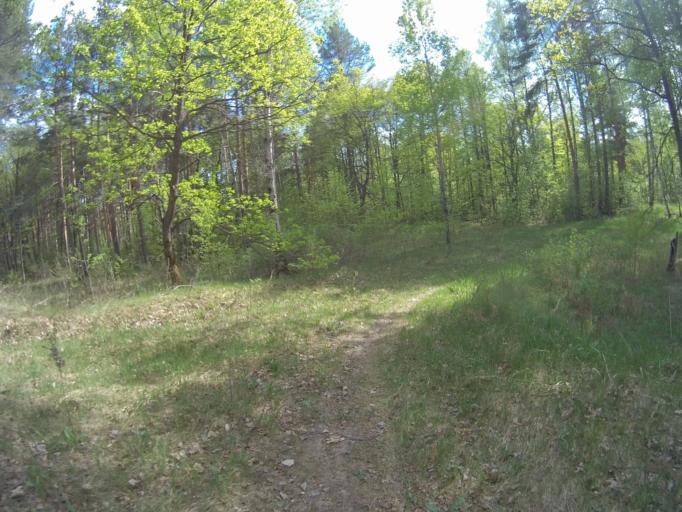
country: RU
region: Vladimir
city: Raduzhnyy
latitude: 56.0468
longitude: 40.3801
